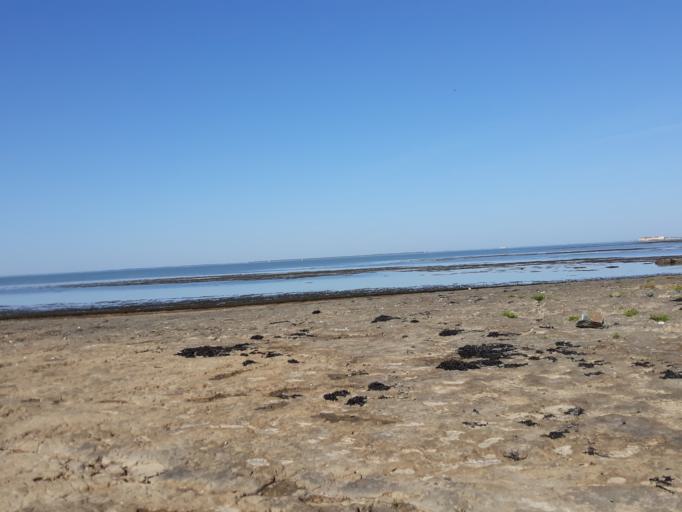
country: FR
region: Poitou-Charentes
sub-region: Departement de la Charente-Maritime
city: Fouras
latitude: 45.9998
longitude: -1.1115
